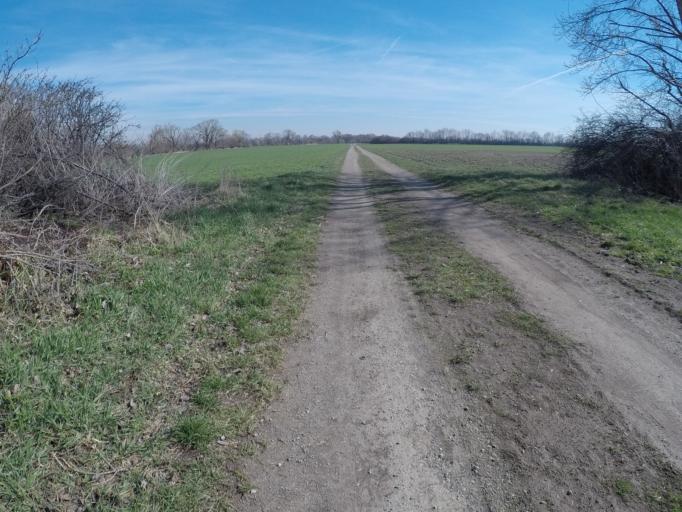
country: AT
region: Lower Austria
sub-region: Politischer Bezirk Modling
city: Biedermannsdorf
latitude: 48.0961
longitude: 16.3358
